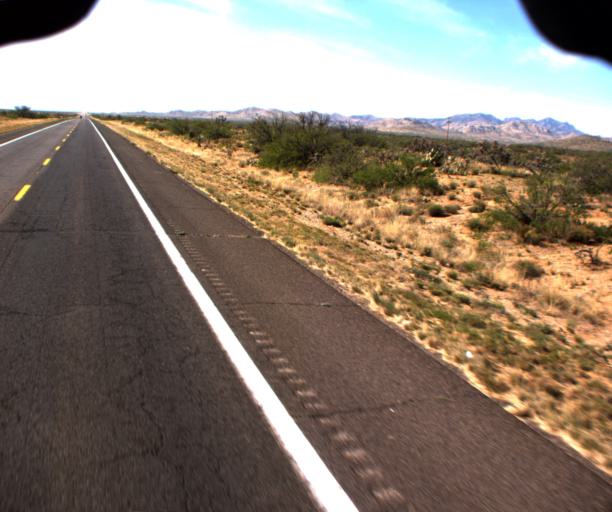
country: US
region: Arizona
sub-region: Graham County
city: Swift Trail Junction
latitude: 32.6119
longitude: -109.6876
